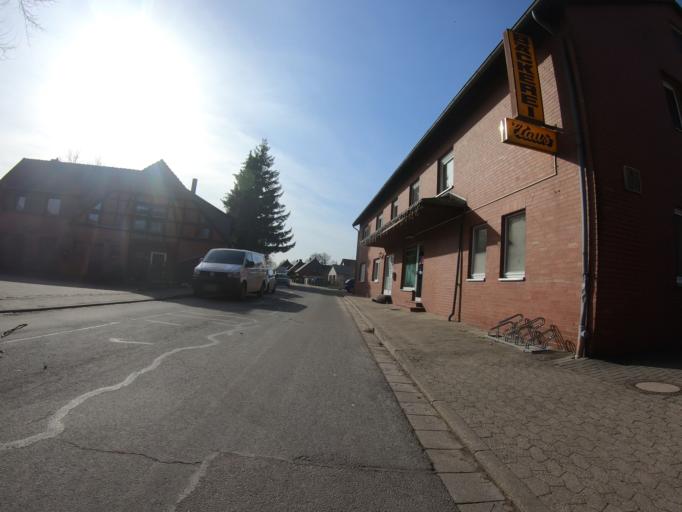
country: DE
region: Lower Saxony
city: Isenbuttel
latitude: 52.4339
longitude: 10.5775
